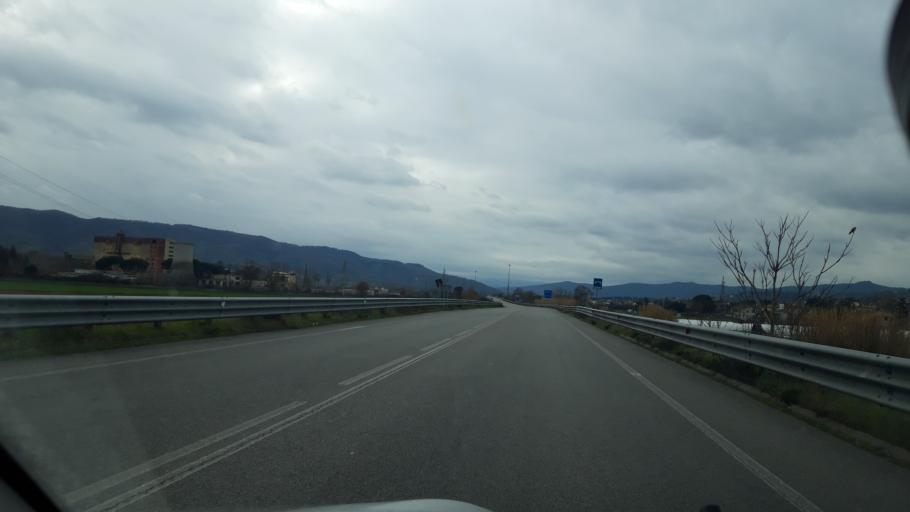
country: IT
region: Umbria
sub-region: Provincia di Perugia
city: Fontignano
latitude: 43.0081
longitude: 12.1876
